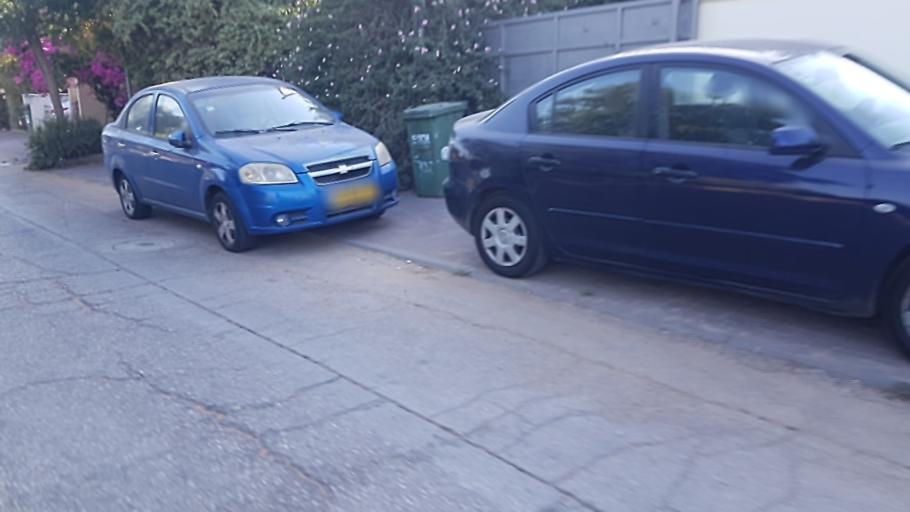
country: IL
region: Central District
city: Hod HaSharon
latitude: 32.1382
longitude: 34.9030
